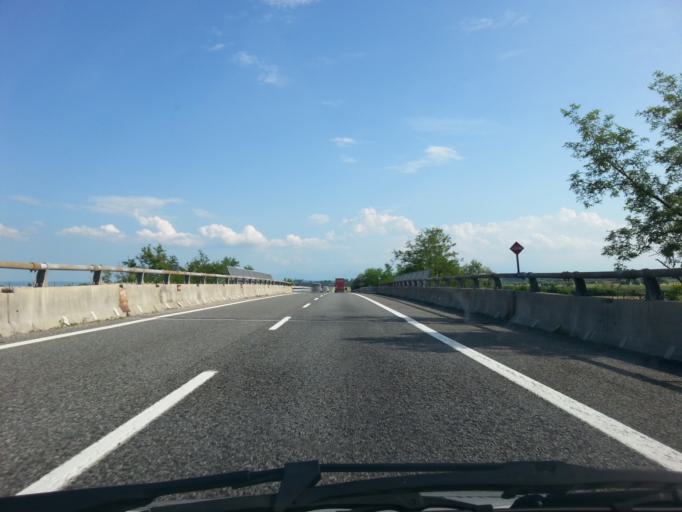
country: IT
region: Piedmont
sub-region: Provincia di Cuneo
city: Marene
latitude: 44.6956
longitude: 7.7654
